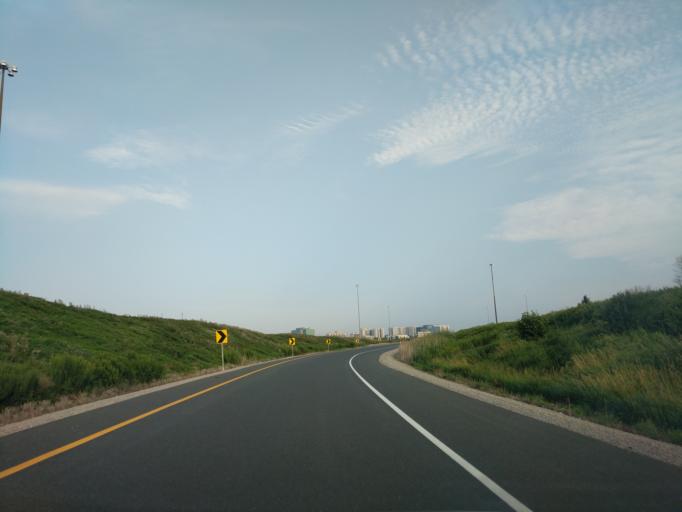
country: CA
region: Ontario
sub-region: York
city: Richmond Hill
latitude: 43.8415
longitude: -79.3651
